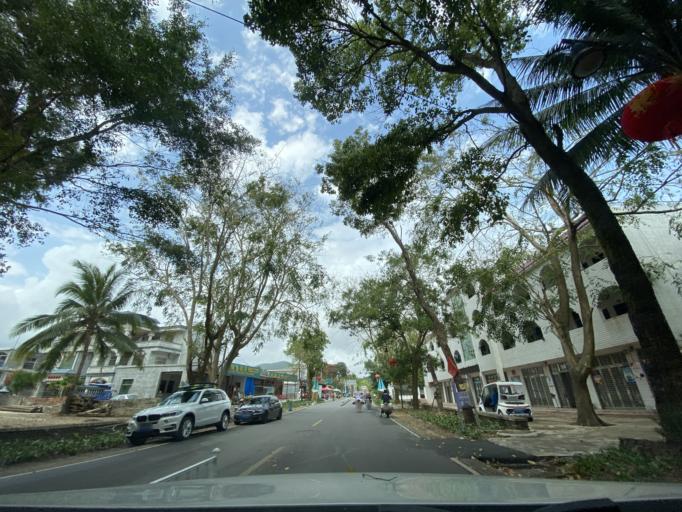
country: CN
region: Hainan
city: Liji
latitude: 18.6679
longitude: 110.2634
